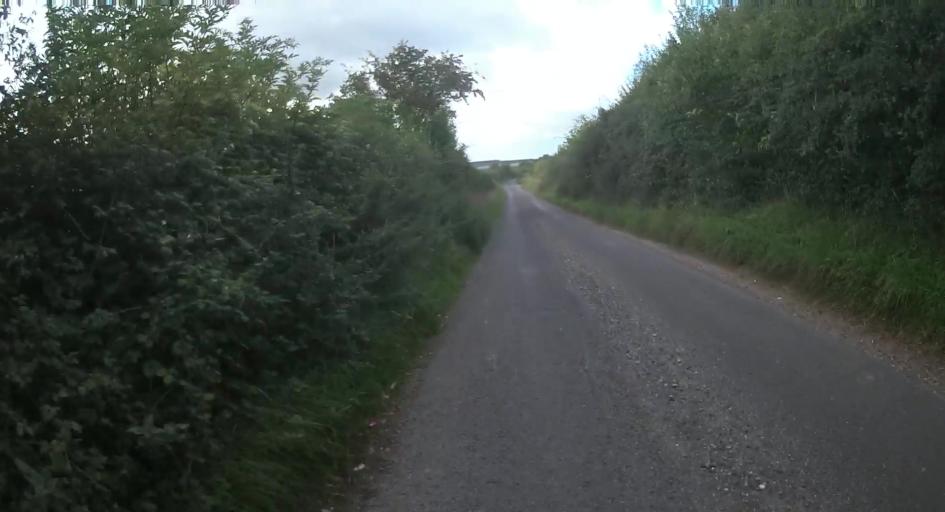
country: GB
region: England
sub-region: Hampshire
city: Overton
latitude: 51.2181
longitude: -1.3196
